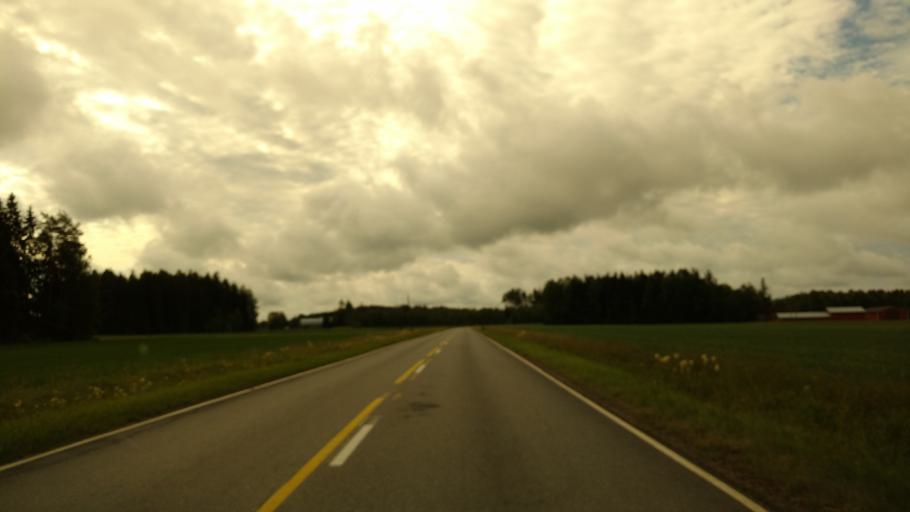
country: FI
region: Varsinais-Suomi
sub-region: Loimaa
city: Koski Tl
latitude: 60.5903
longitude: 23.1323
